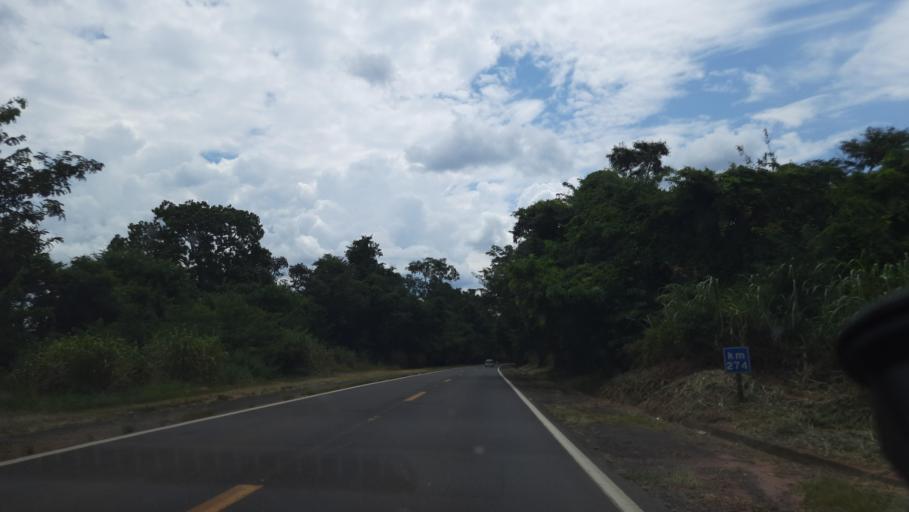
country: BR
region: Sao Paulo
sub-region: Mococa
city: Mococa
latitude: -21.4937
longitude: -47.0720
